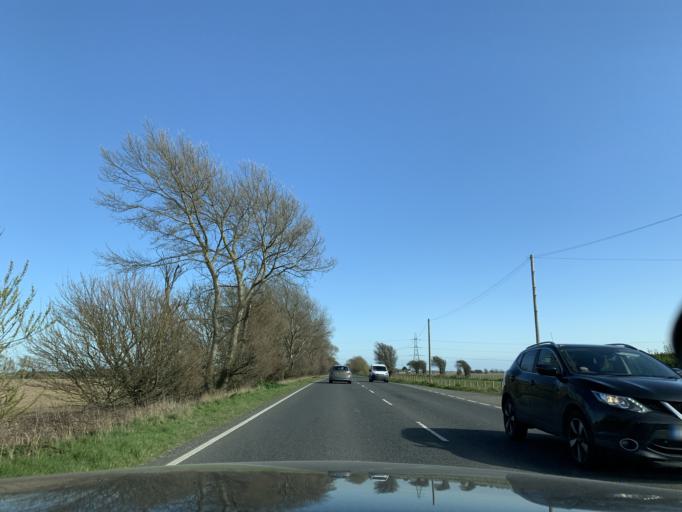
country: GB
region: England
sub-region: Kent
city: New Romney
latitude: 50.9880
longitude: 0.9048
